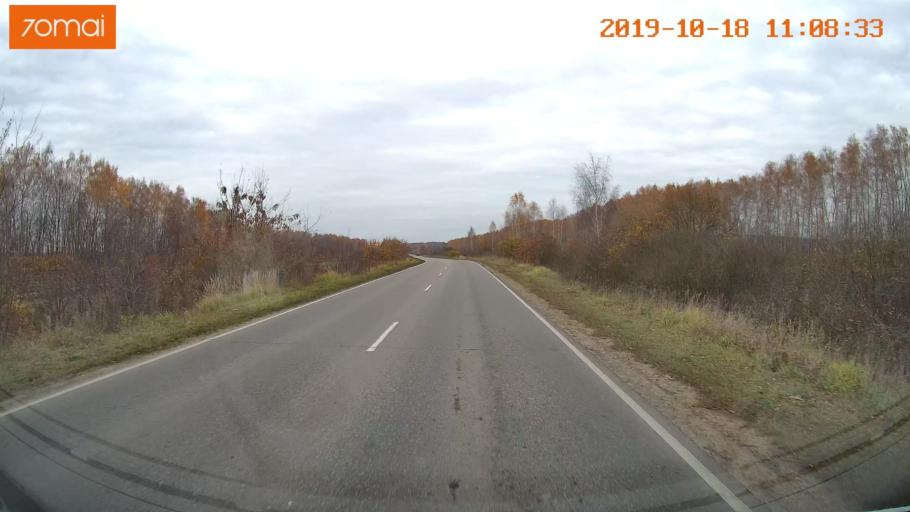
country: RU
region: Tula
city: Kimovsk
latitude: 53.9398
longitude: 38.5367
